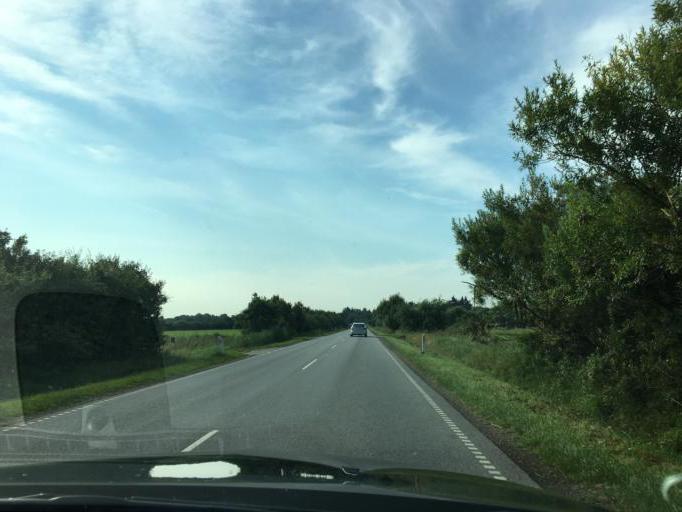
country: DK
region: South Denmark
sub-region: Varde Kommune
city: Oksbol
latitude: 55.7954
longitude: 8.2339
